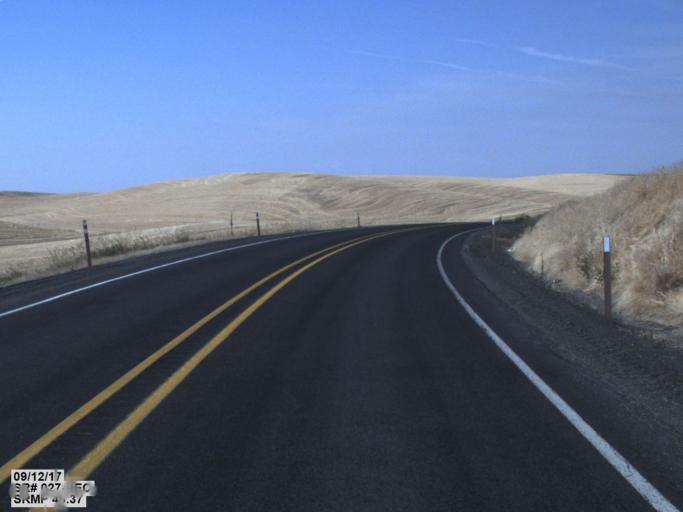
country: US
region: Idaho
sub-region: Benewah County
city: Plummer
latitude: 47.1935
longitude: -117.1083
